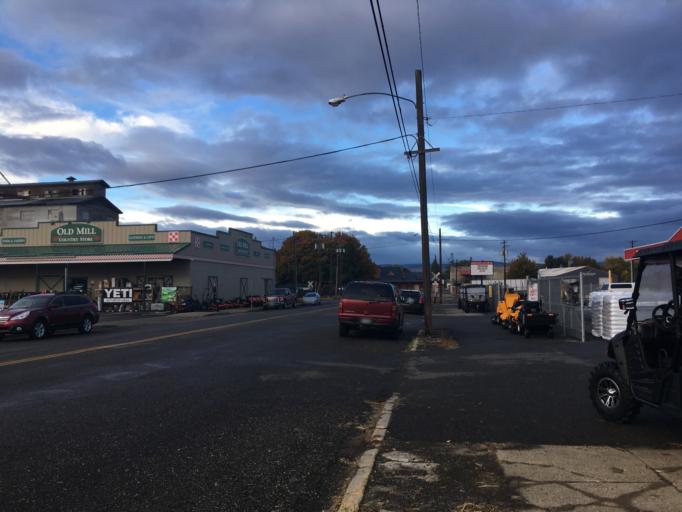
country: US
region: Washington
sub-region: Kittitas County
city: Ellensburg
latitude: 46.9944
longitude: -120.5523
